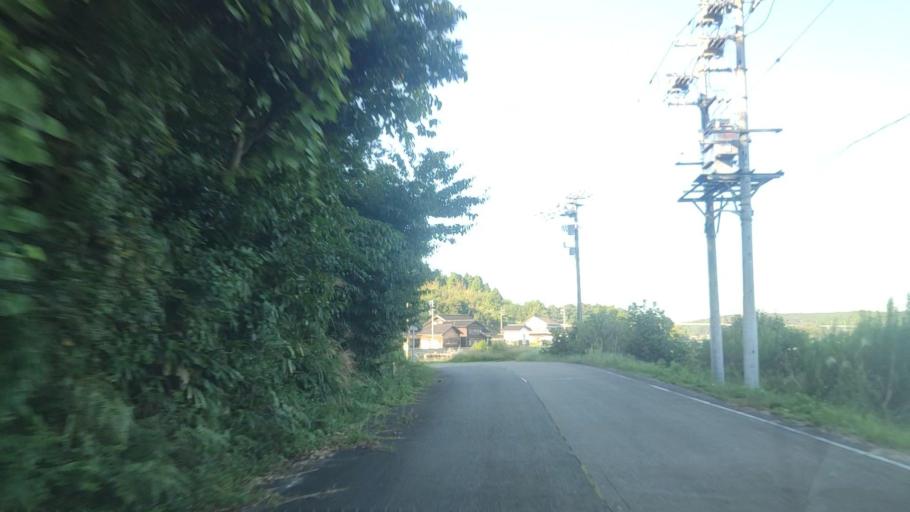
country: JP
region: Ishikawa
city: Nanao
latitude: 37.1272
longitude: 136.8961
